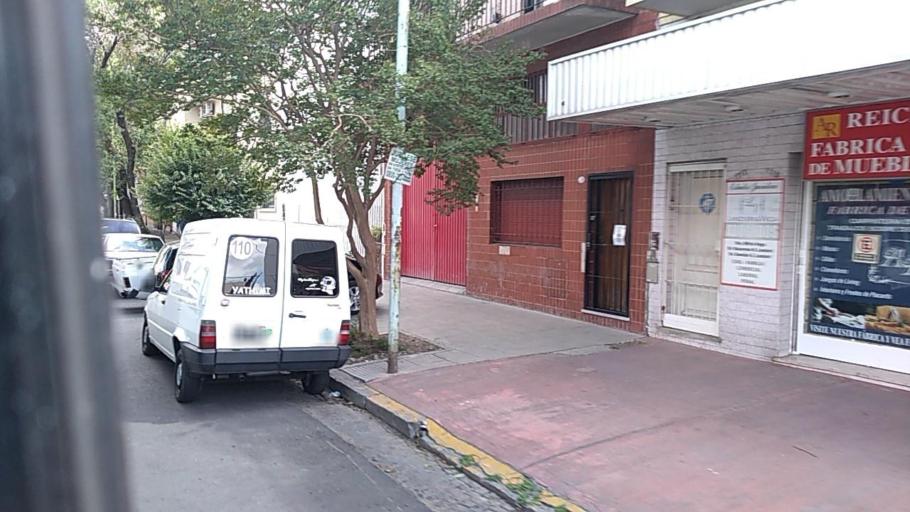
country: AR
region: Buenos Aires F.D.
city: Villa Santa Rita
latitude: -34.6222
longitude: -58.5059
